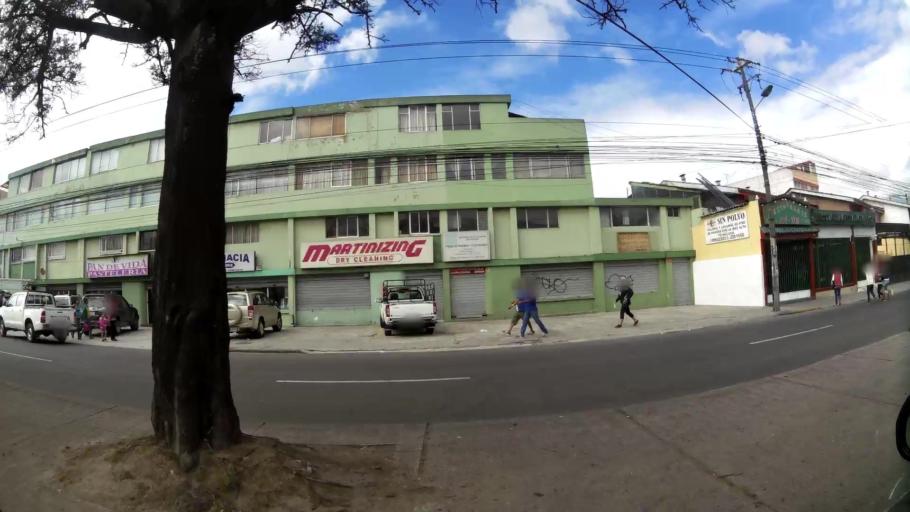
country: EC
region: Pichincha
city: Quito
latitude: -0.1543
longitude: -78.4753
